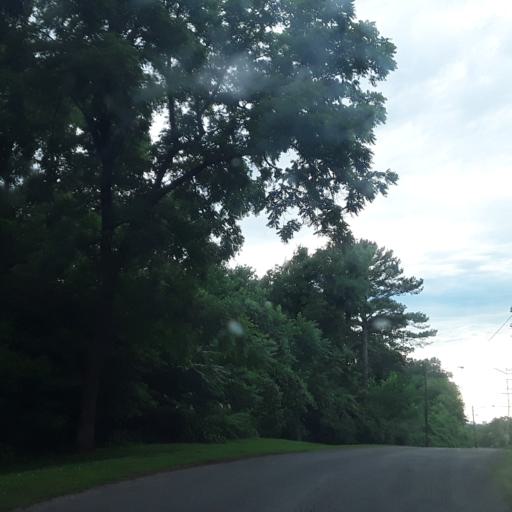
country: US
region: Tennessee
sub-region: Wilson County
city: Green Hill
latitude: 36.1624
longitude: -86.6019
